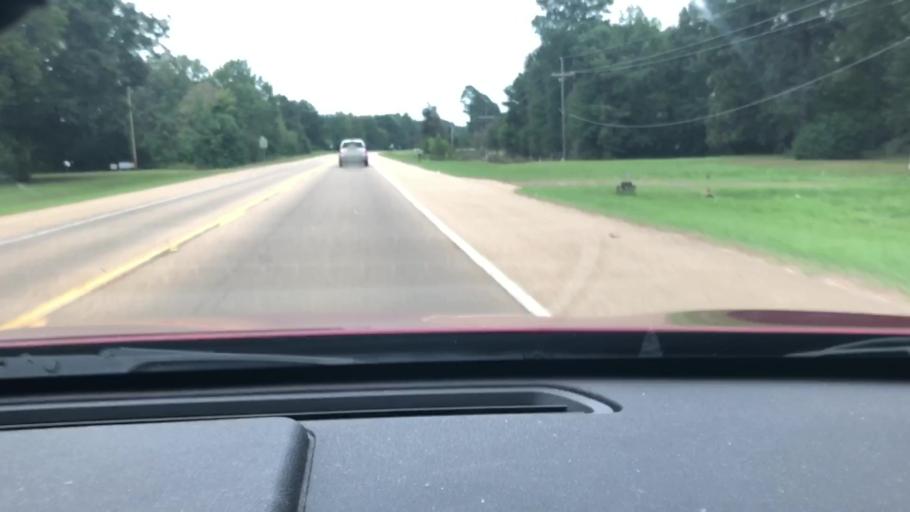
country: US
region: Arkansas
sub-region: Lafayette County
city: Stamps
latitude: 33.3649
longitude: -93.4787
